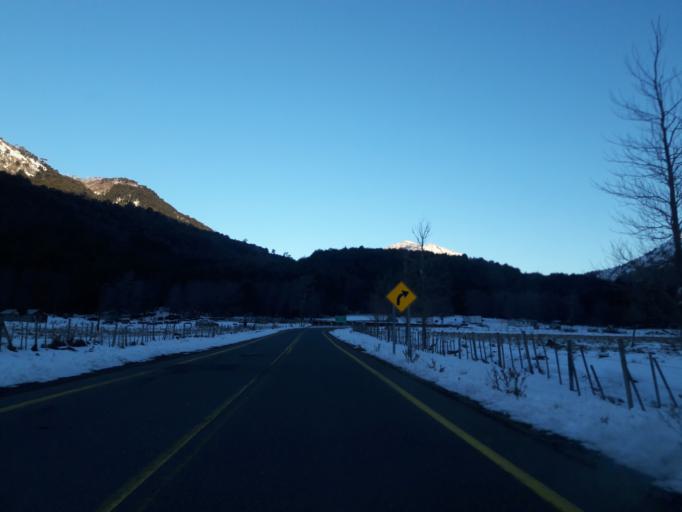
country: CL
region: Araucania
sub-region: Provincia de Cautin
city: Vilcun
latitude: -38.4988
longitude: -71.5205
